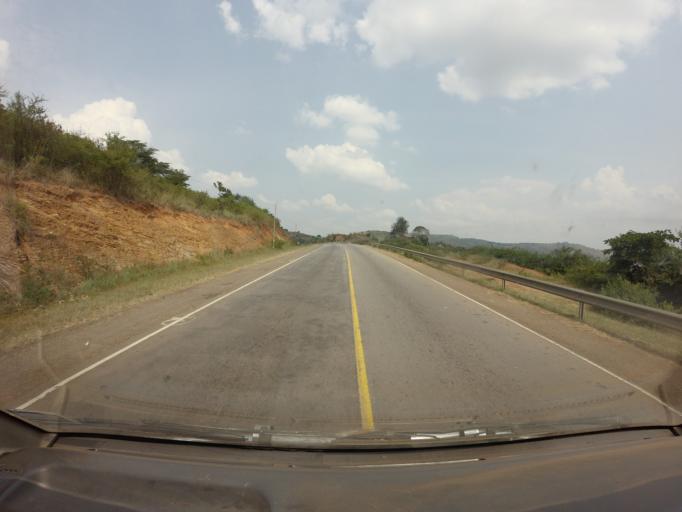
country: UG
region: Central Region
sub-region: Lyantonde District
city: Lyantonde
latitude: -0.3758
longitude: 31.2778
